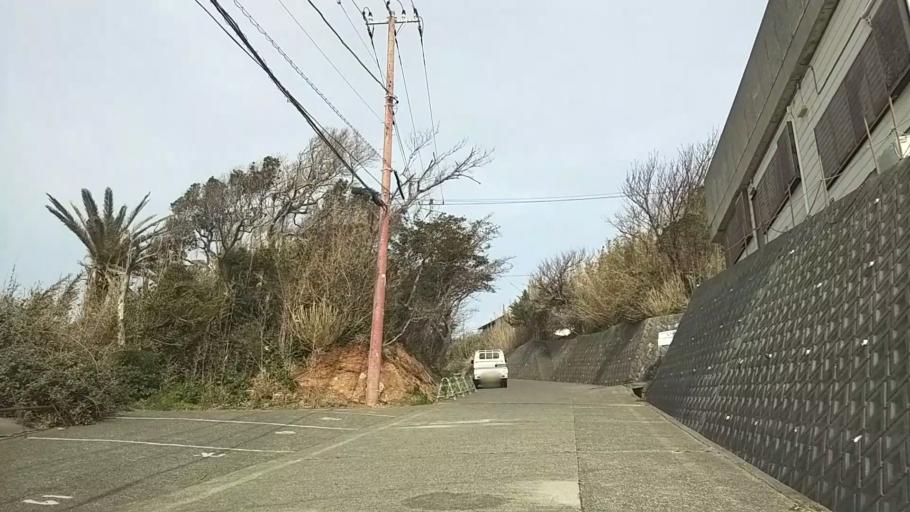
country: JP
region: Shizuoka
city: Shimoda
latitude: 34.6537
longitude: 138.9651
